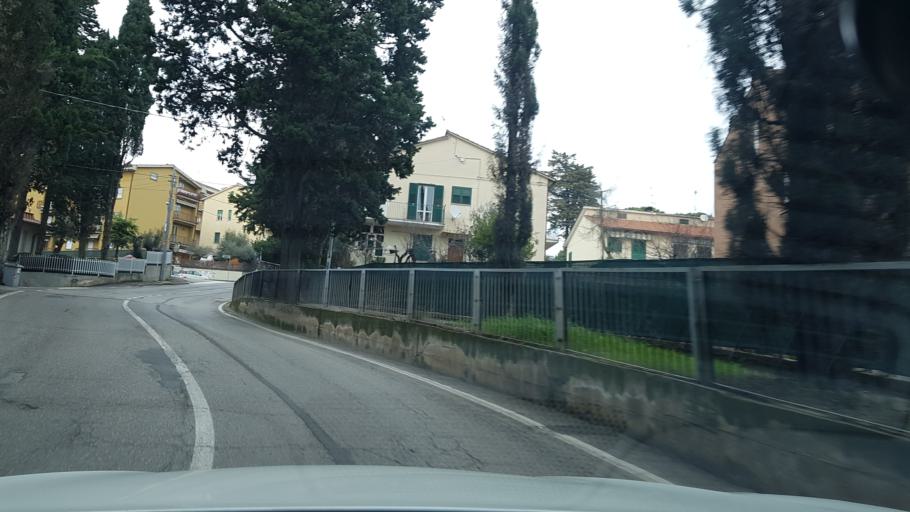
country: IT
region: Umbria
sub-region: Provincia di Perugia
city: Perugia
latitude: 43.1164
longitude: 12.3650
